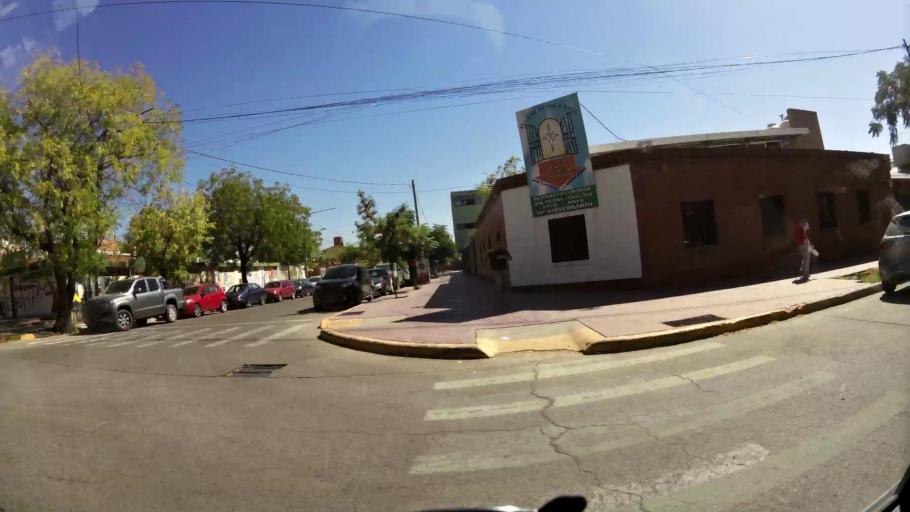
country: AR
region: Mendoza
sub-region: Departamento de Godoy Cruz
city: Godoy Cruz
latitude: -32.9066
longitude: -68.8620
